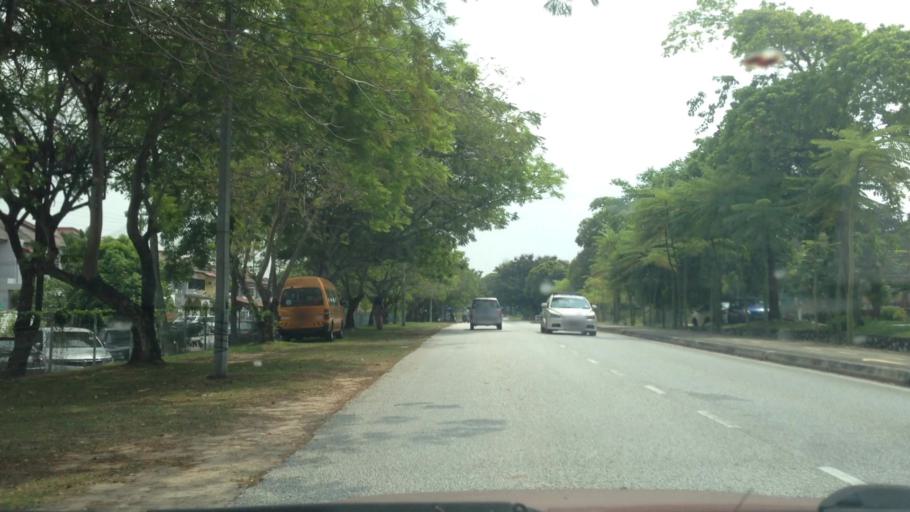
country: MY
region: Selangor
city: Subang Jaya
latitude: 3.0469
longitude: 101.5739
